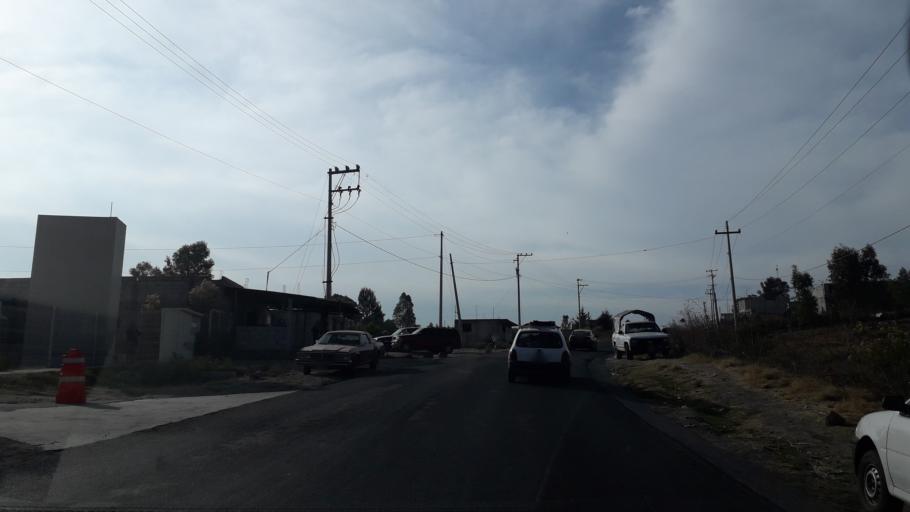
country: MX
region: Puebla
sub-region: Puebla
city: San Andres Azumiatla
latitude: 18.9130
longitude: -98.2427
